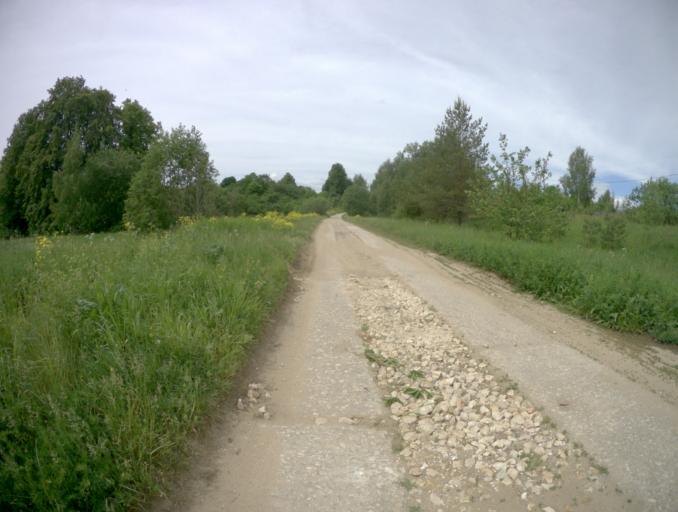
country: RU
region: Vladimir
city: Stavrovo
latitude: 56.1865
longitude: 39.9538
